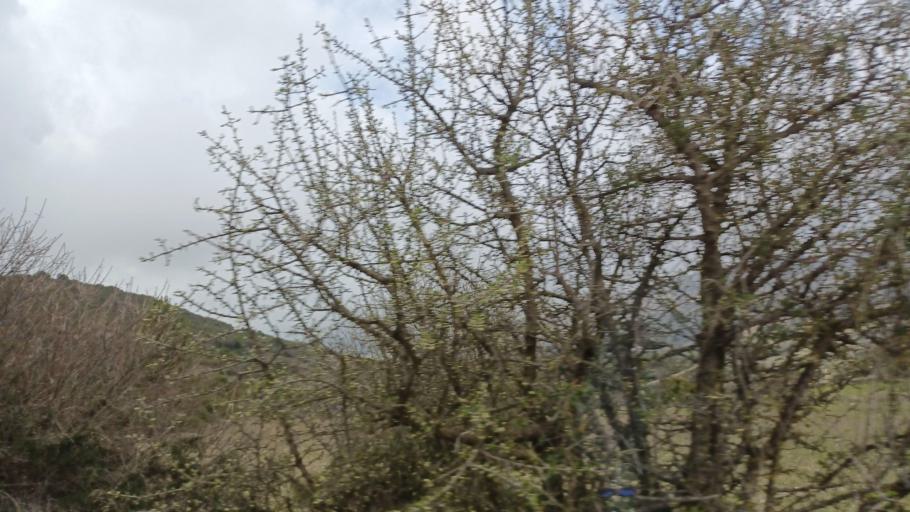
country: CY
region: Limassol
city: Pachna
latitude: 34.7700
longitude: 32.8319
